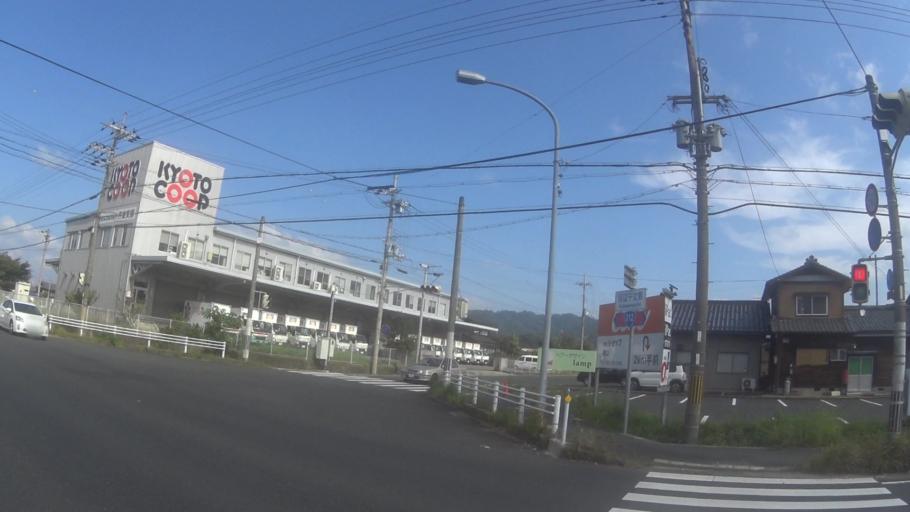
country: JP
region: Kyoto
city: Miyazu
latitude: 35.5980
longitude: 135.0886
